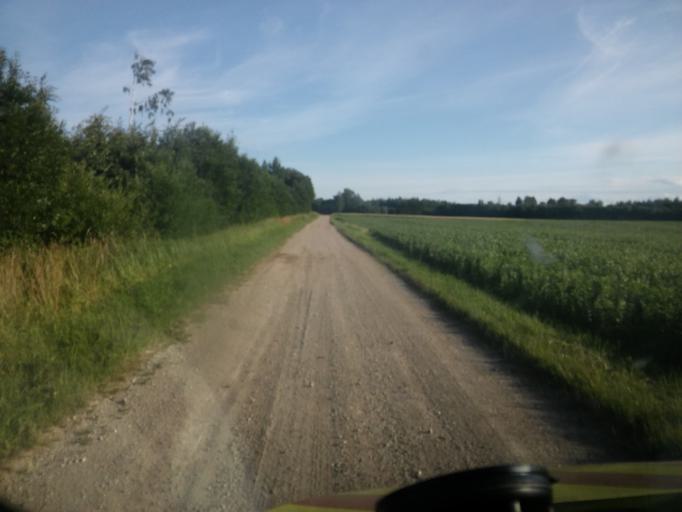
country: EE
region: Valgamaa
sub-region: Torva linn
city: Torva
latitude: 58.1013
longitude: 26.0027
